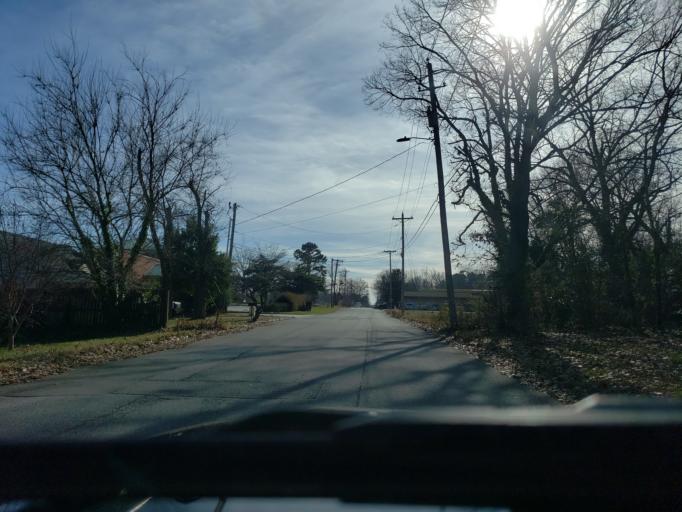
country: US
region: North Carolina
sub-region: Cleveland County
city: Kings Mountain
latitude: 35.2419
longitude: -81.3303
